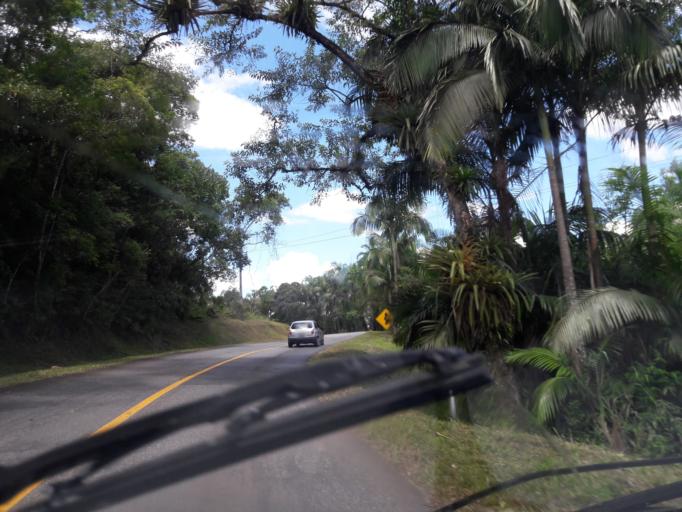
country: BR
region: Parana
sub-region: Antonina
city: Antonina
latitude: -25.4215
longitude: -48.8226
